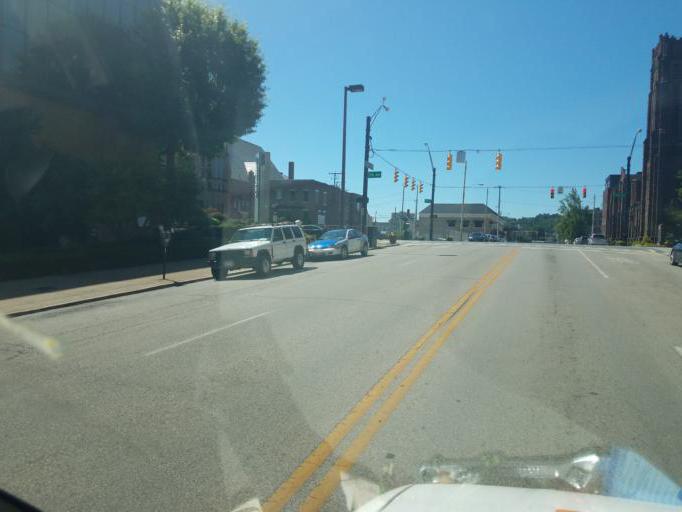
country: US
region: West Virginia
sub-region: Cabell County
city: Huntington
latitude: 38.4201
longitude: -82.4419
